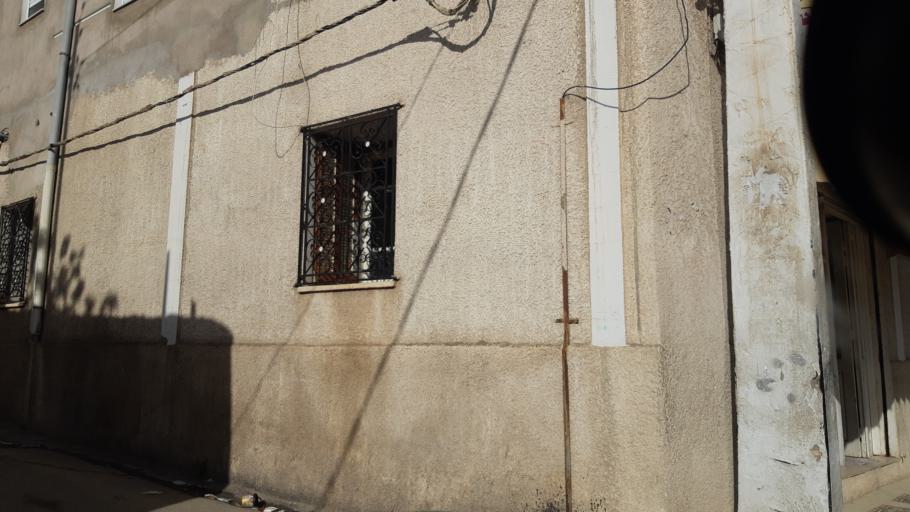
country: TN
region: Susah
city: Akouda
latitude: 35.8730
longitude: 10.5372
